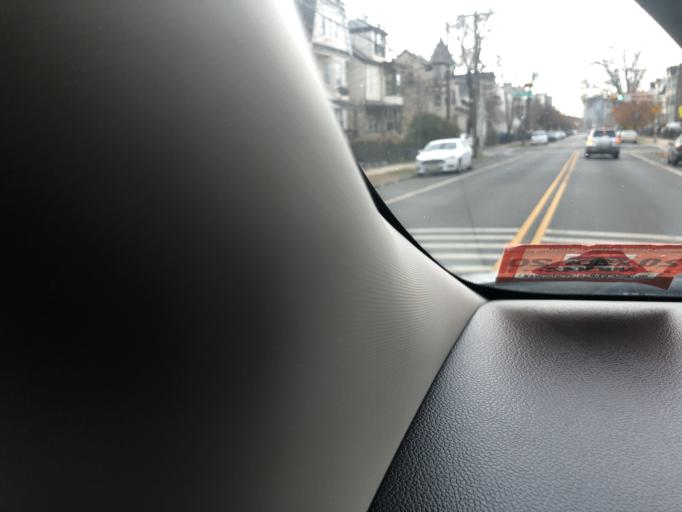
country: US
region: New Jersey
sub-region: Essex County
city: Newark
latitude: 40.7185
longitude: -74.1948
